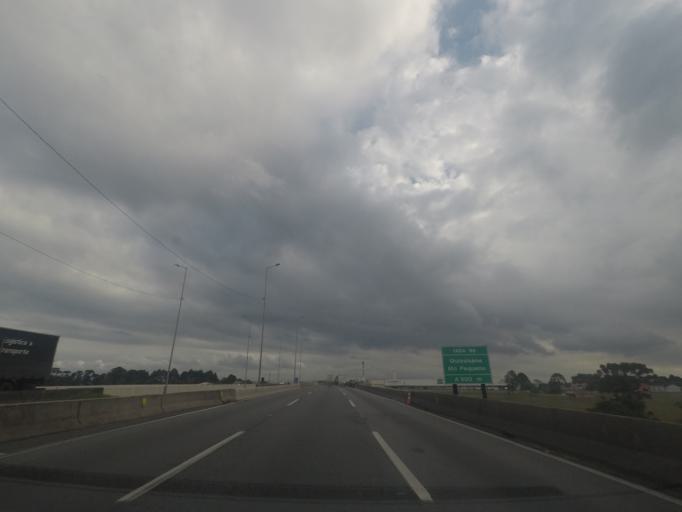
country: BR
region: Parana
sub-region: Sao Jose Dos Pinhais
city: Sao Jose dos Pinhais
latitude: -25.5340
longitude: -49.1467
